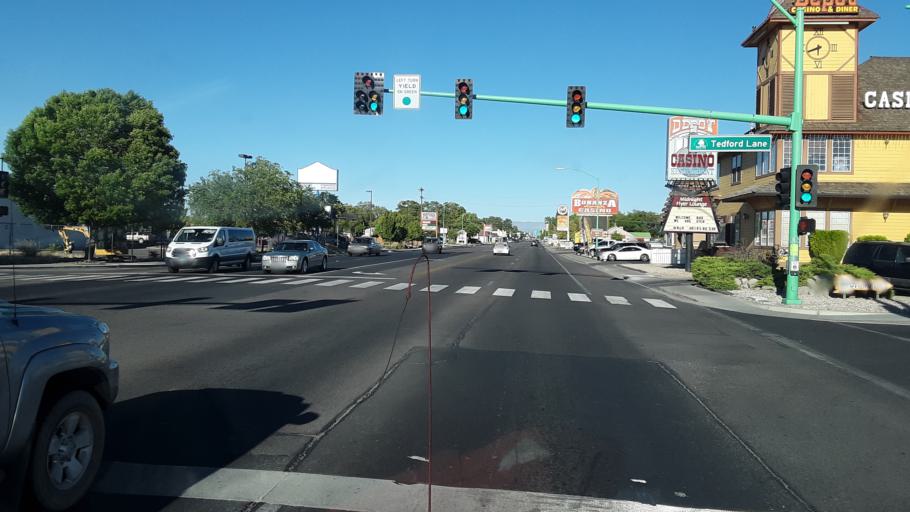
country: US
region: Nevada
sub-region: Churchill County
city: Fallon
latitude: 39.4748
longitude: -118.7883
